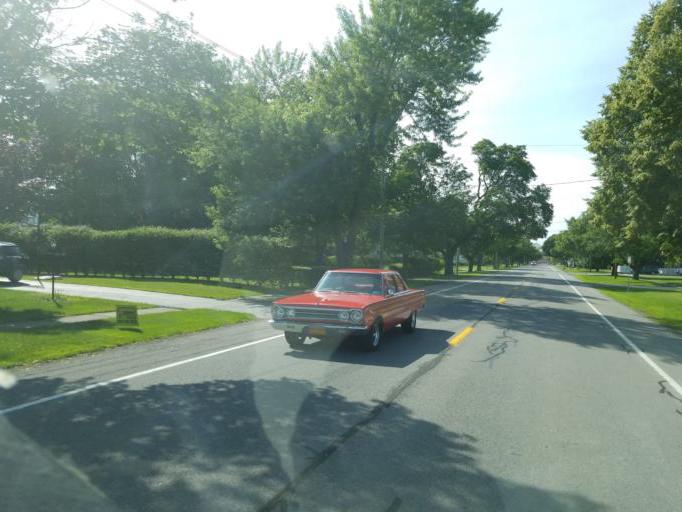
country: US
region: New York
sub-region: Livingston County
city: Caledonia
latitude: 42.9681
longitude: -77.8472
